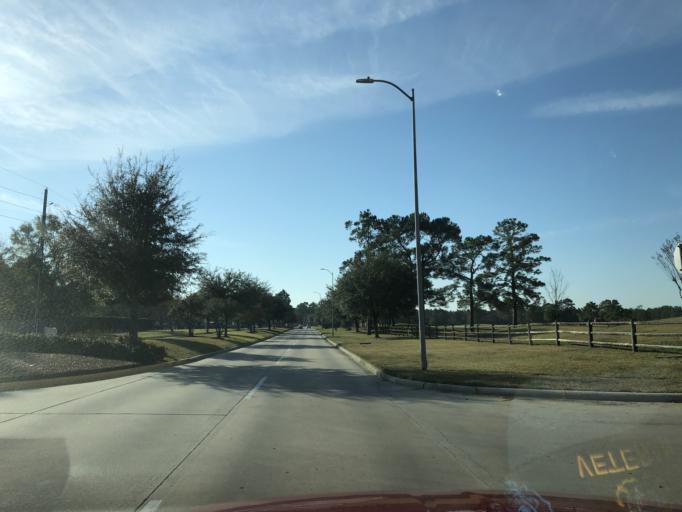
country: US
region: Texas
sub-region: Harris County
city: Tomball
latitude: 30.0440
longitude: -95.5629
